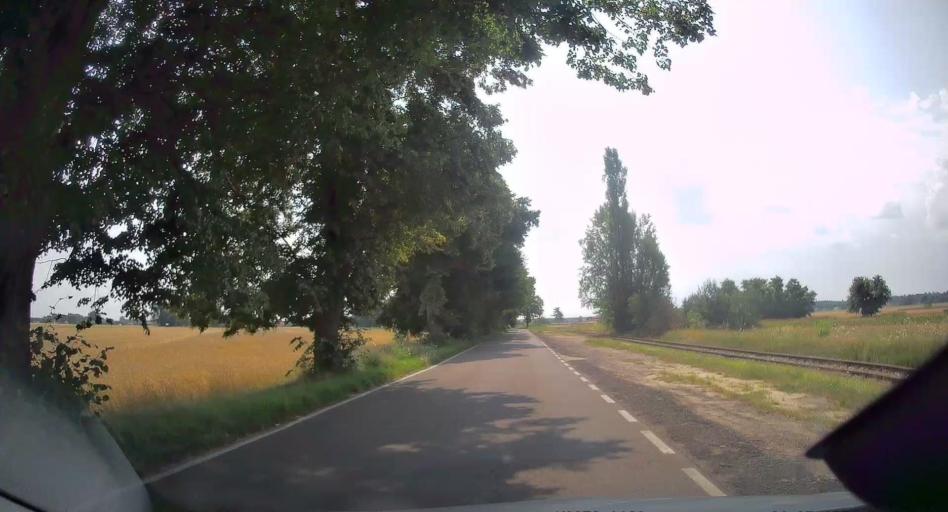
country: PL
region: Lodz Voivodeship
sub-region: Powiat tomaszowski
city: Lubochnia
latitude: 51.5712
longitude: 20.0994
